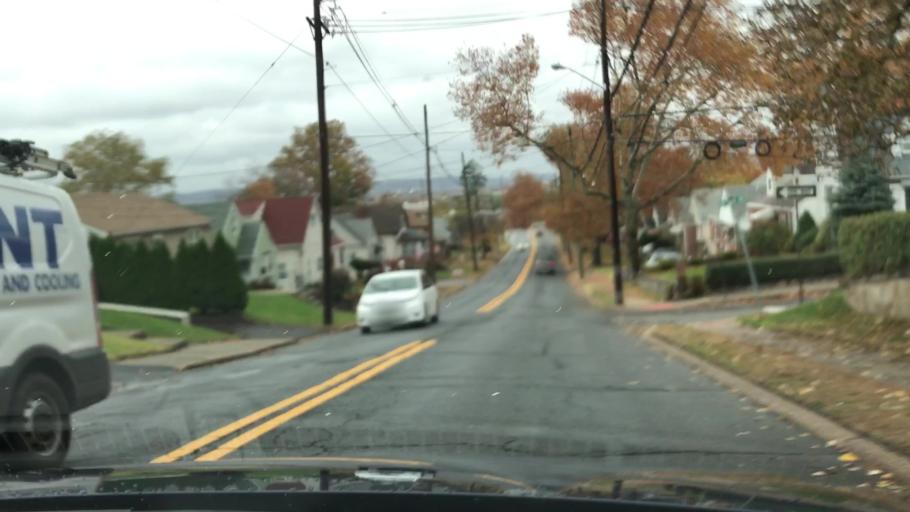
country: US
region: New Jersey
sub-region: Bergen County
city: Hasbrouck Heights
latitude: 40.8597
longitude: -74.0846
